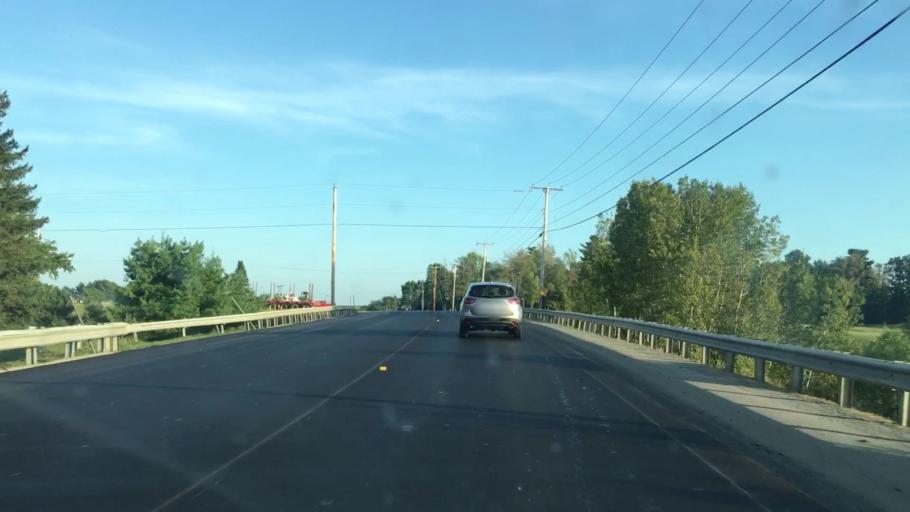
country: US
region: Maine
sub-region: Penobscot County
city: Hampden
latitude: 44.7678
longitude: -68.8555
